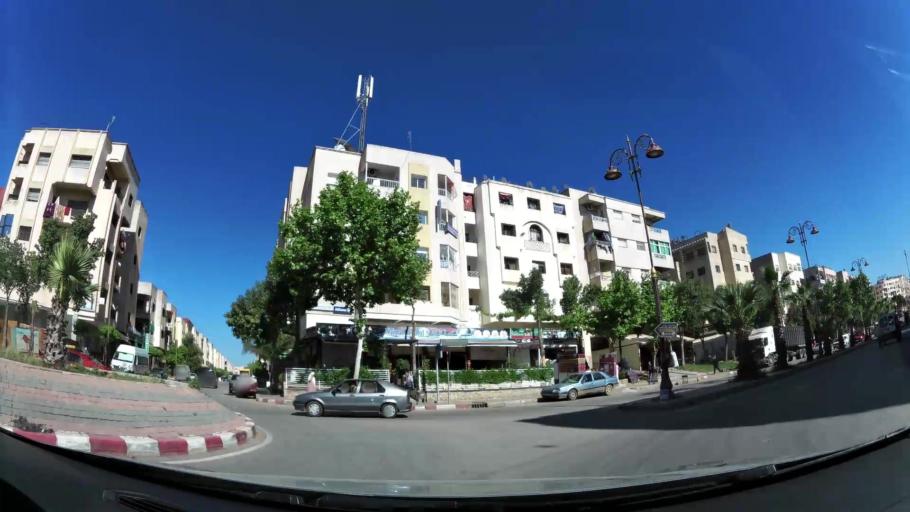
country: MA
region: Fes-Boulemane
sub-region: Fes
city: Fes
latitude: 34.0170
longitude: -4.9705
